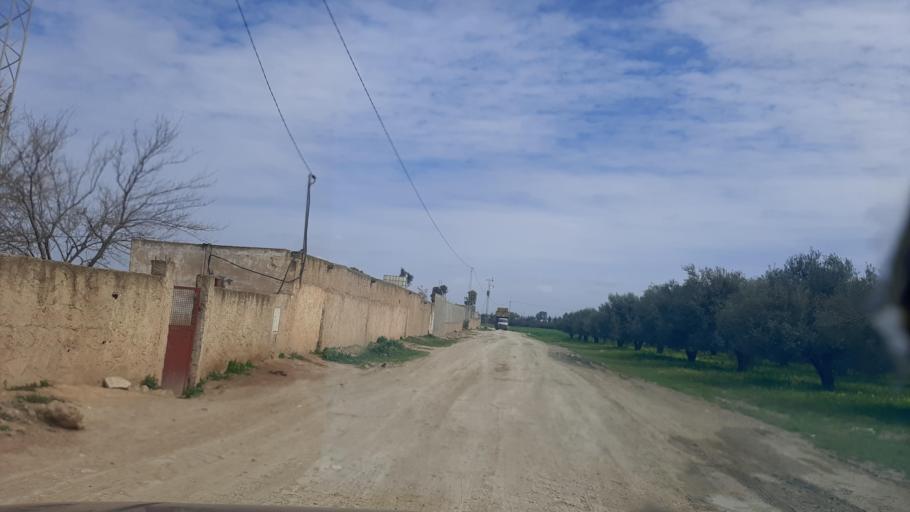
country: TN
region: Tunis
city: Oued Lill
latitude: 36.6949
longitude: 9.9992
